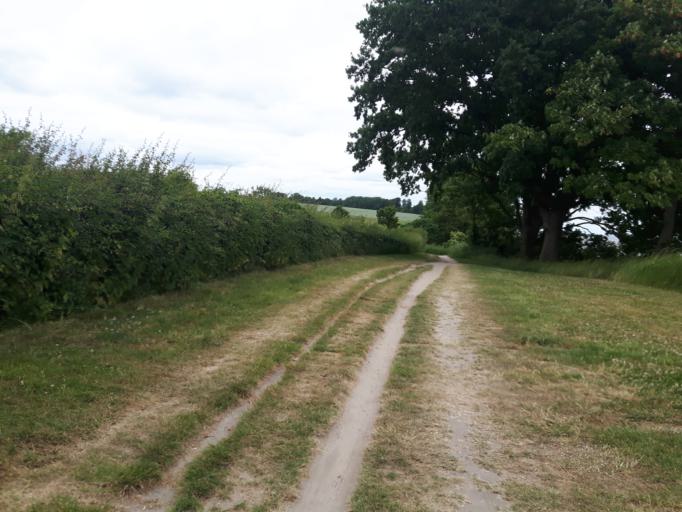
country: DE
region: Schleswig-Holstein
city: Schashagen
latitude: 54.1069
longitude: 10.9055
